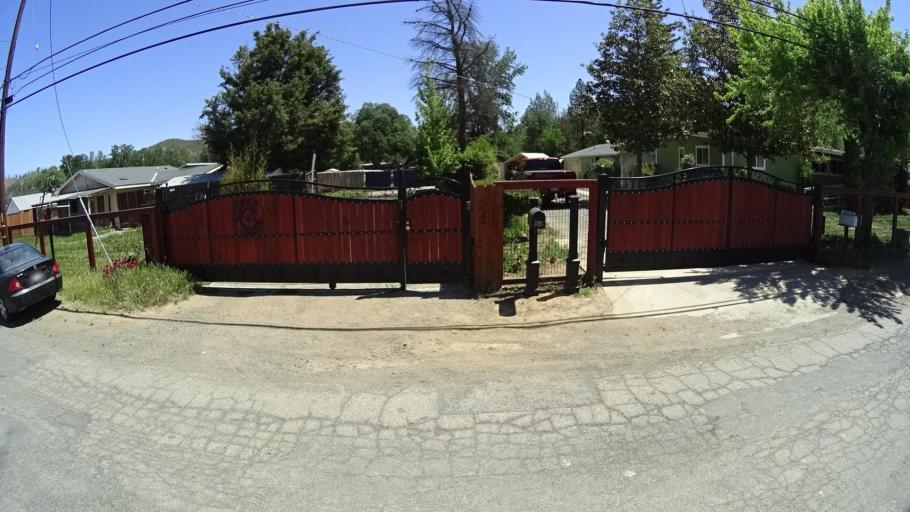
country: US
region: California
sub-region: Lake County
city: Lower Lake
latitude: 38.9132
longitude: -122.5901
